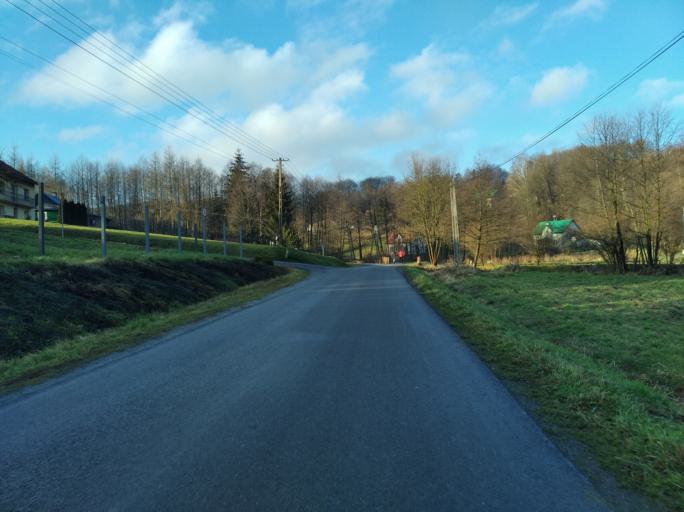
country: PL
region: Subcarpathian Voivodeship
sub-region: Powiat strzyzowski
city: Czudec
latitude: 49.9472
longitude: 21.8049
